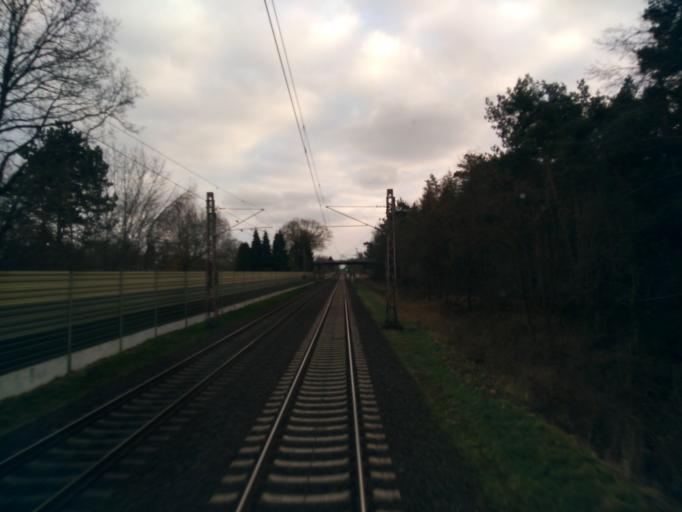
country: DE
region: Lower Saxony
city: Jelmstorf
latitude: 53.1100
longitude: 10.5378
